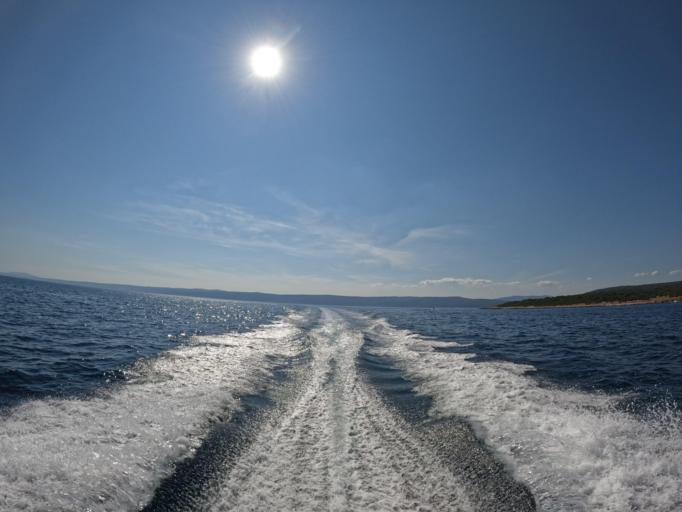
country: HR
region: Primorsko-Goranska
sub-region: Grad Krk
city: Krk
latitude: 44.9513
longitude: 14.5484
